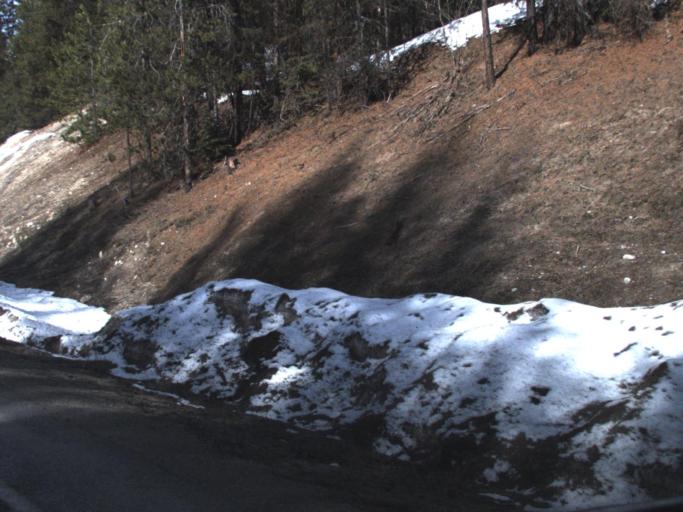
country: US
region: Washington
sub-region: Stevens County
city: Colville
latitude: 48.6409
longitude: -117.5202
